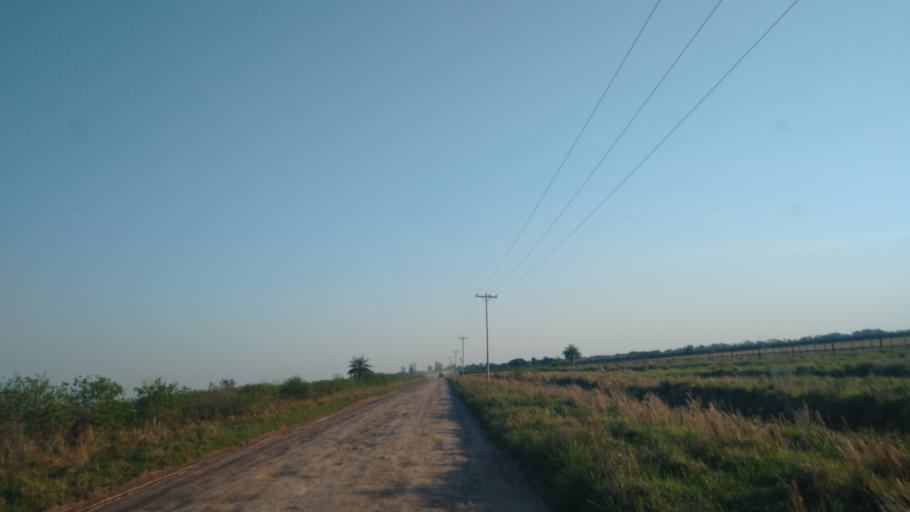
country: PY
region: Neembucu
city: Cerrito
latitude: -27.3851
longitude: -57.6572
